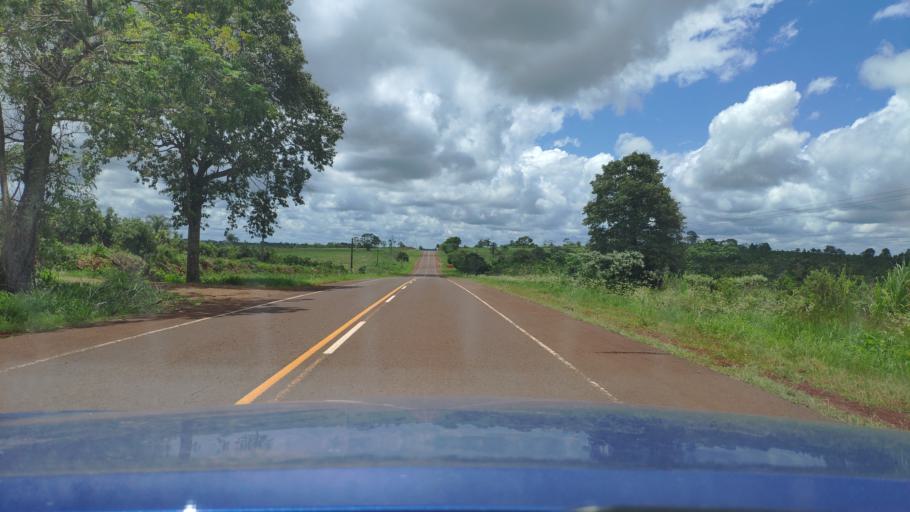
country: AR
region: Misiones
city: Picada Gobernador Lopez
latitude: -27.6769
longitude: -55.2805
